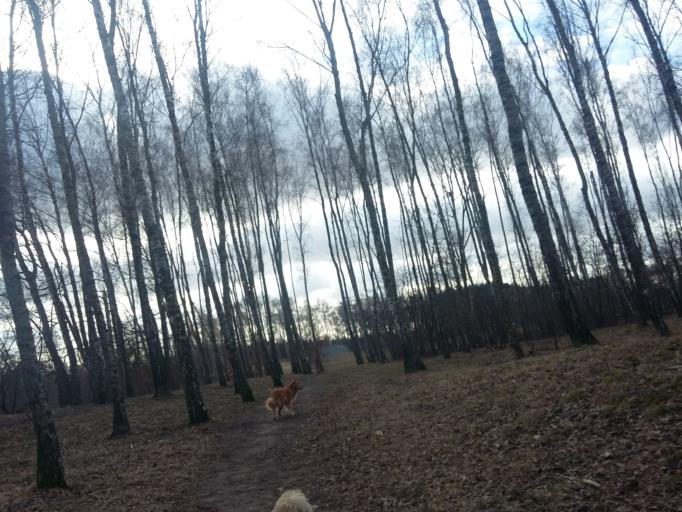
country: PL
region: Lodz Voivodeship
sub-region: Powiat pabianicki
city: Ksawerow
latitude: 51.7276
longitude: 19.4183
